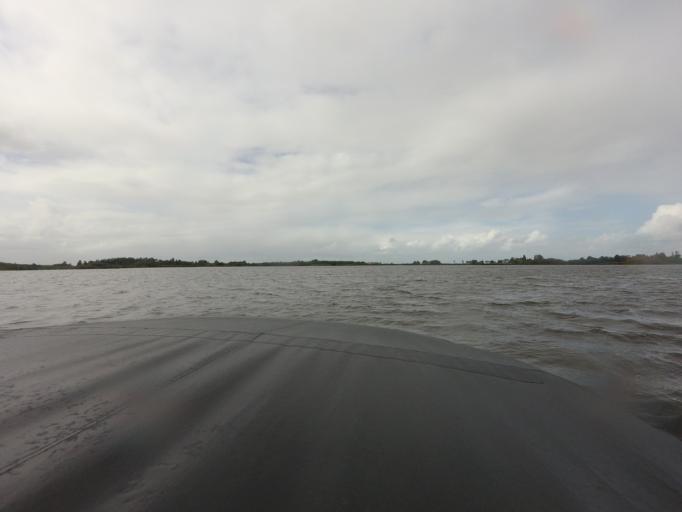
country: NL
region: Friesland
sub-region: Gemeente Boarnsterhim
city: Warten
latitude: 53.1337
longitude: 5.8982
